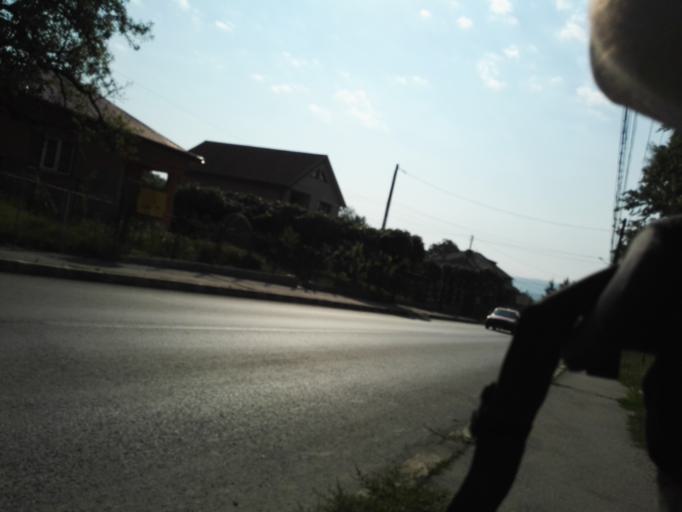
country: RO
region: Suceava
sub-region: Municipiul Falticeni
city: Falticeni
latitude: 47.4650
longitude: 26.2882
